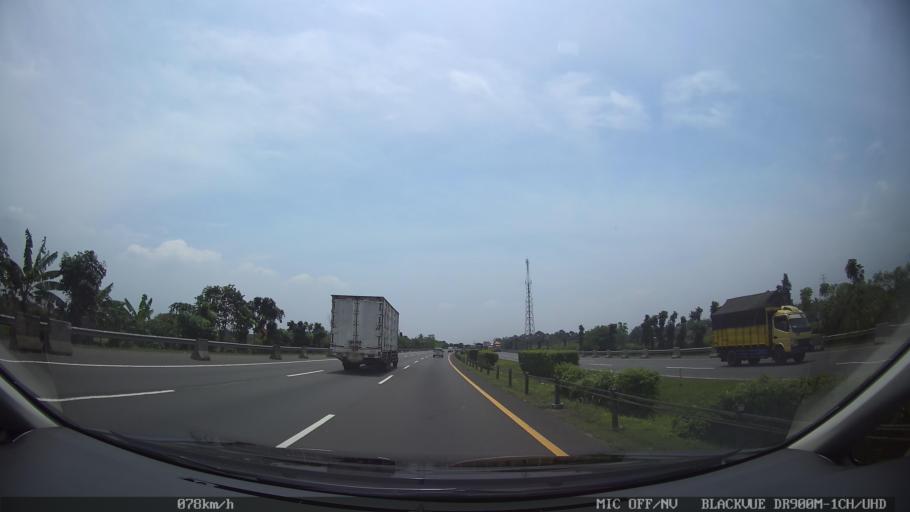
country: ID
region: West Java
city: Kresek
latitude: -6.1909
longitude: 106.4131
